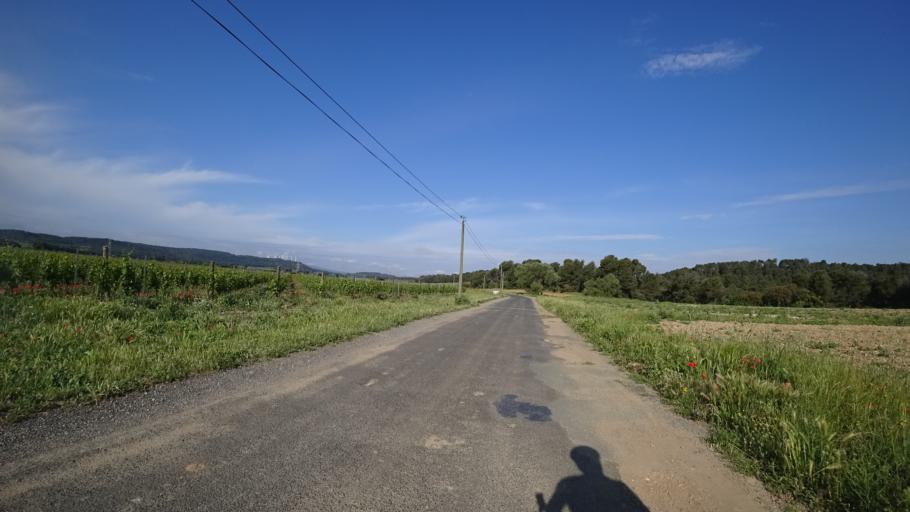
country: FR
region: Languedoc-Roussillon
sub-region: Departement de l'Aude
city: Lezignan-Corbieres
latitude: 43.2360
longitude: 2.7552
